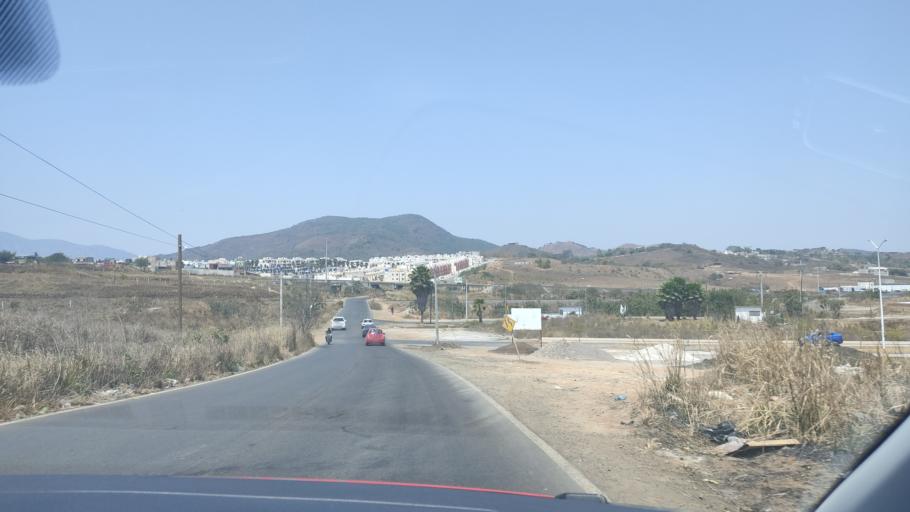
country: MX
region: Nayarit
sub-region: Tepic
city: La Corregidora
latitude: 21.4917
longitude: -104.8108
